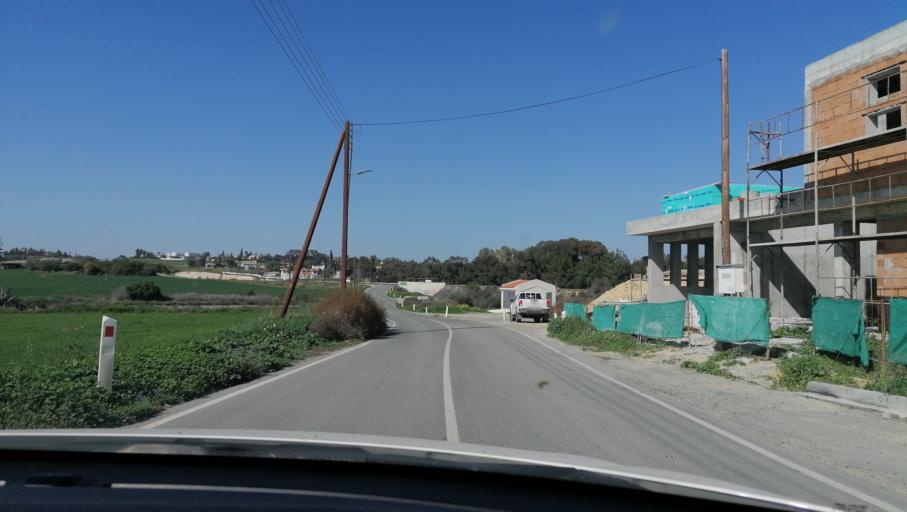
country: CY
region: Lefkosia
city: Geri
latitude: 35.1194
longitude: 33.4007
